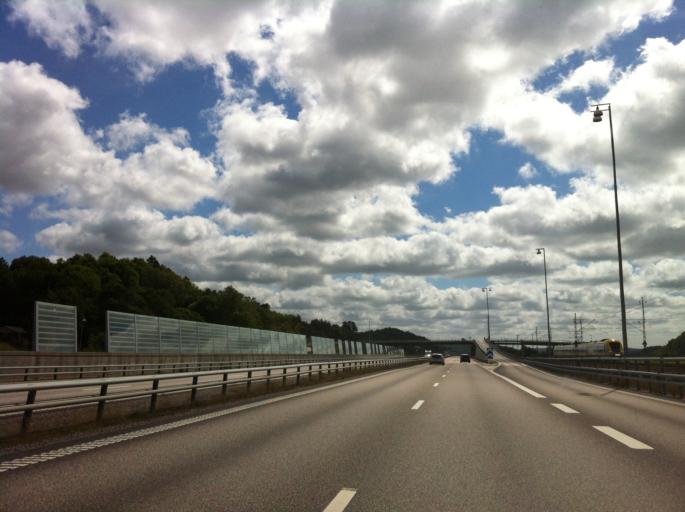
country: SE
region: Vaestra Goetaland
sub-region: Ale Kommun
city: Nodinge-Nol
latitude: 57.9212
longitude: 12.0646
